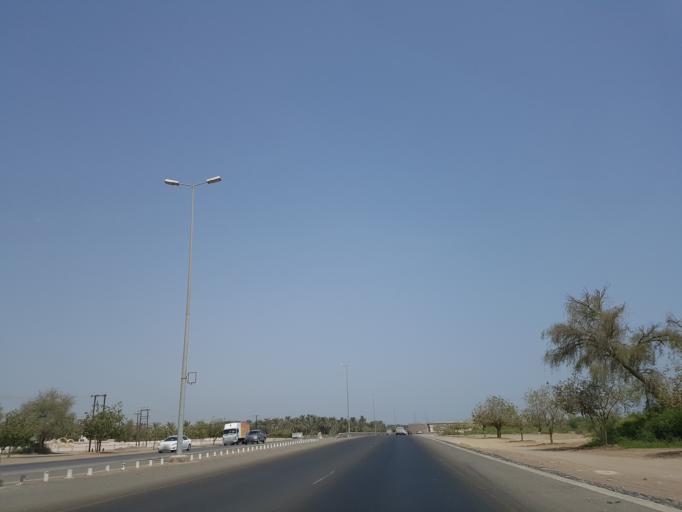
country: OM
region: Al Batinah
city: Saham
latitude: 24.1754
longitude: 56.8582
